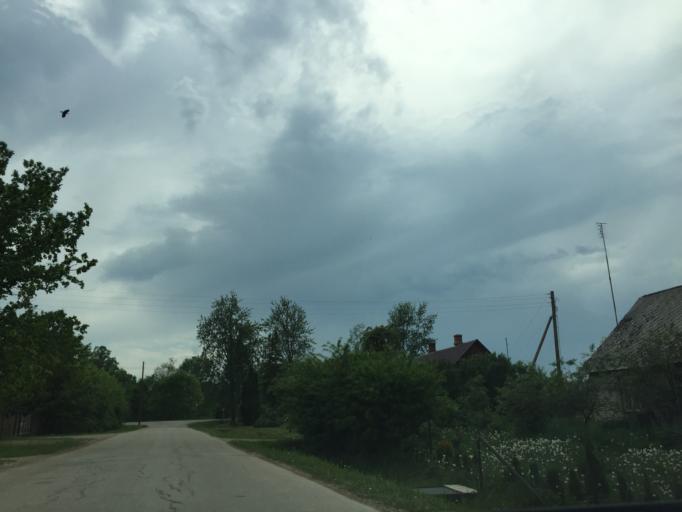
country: LV
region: Livani
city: Livani
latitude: 56.5361
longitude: 26.2409
